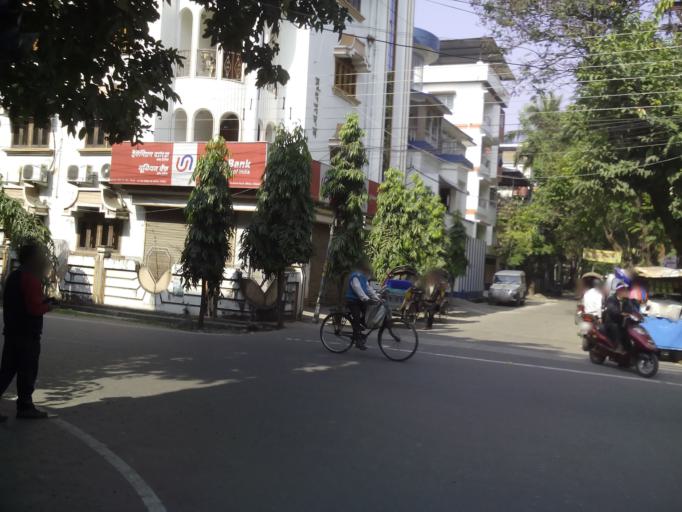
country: IN
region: West Bengal
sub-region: Darjiling
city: Shiliguri
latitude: 26.7095
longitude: 88.4340
